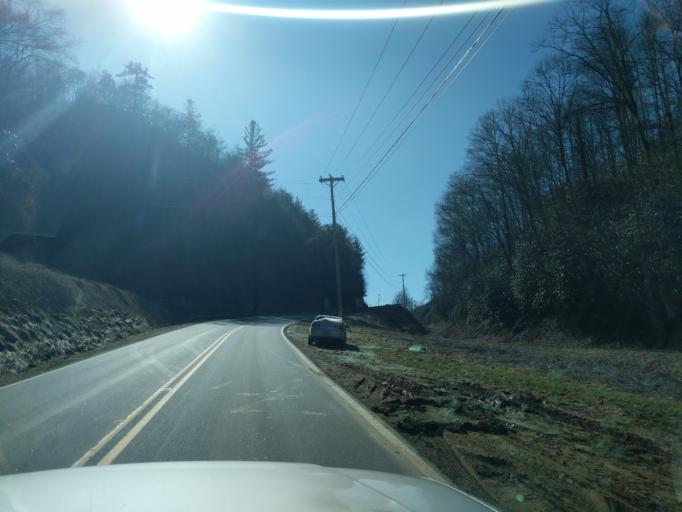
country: US
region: North Carolina
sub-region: Graham County
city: Robbinsville
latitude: 35.2514
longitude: -83.7001
